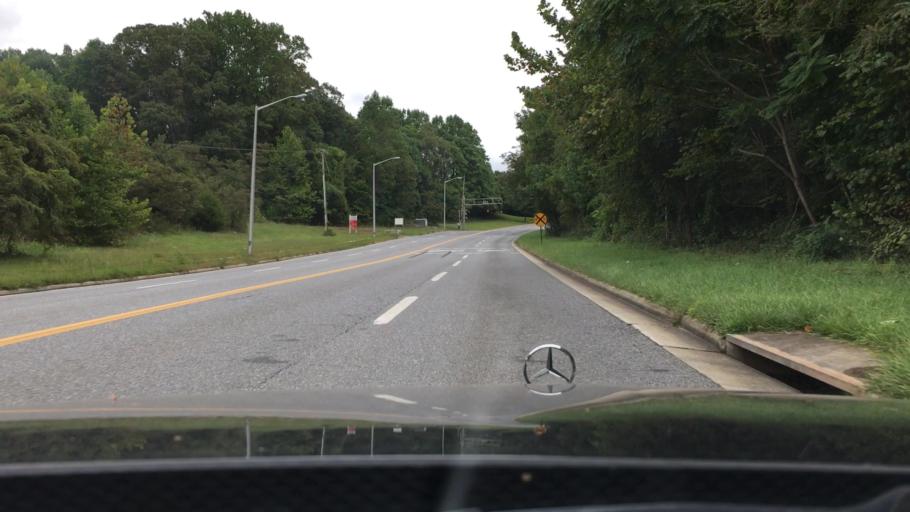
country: US
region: Virginia
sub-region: City of Lynchburg
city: West Lynchburg
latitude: 37.3990
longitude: -79.2321
